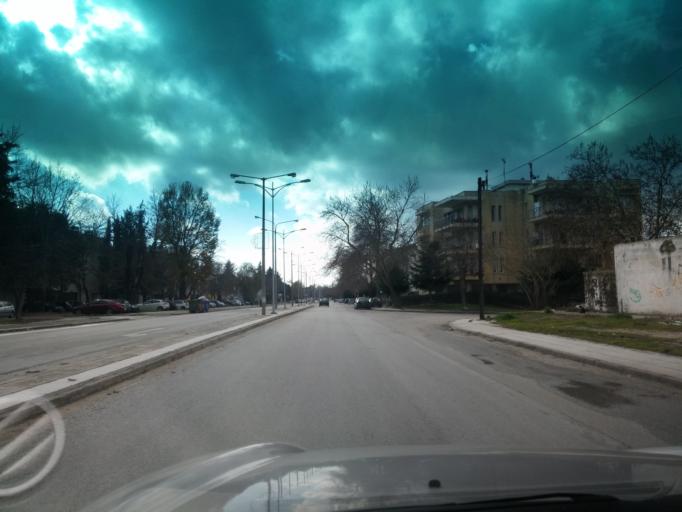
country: GR
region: East Macedonia and Thrace
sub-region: Nomos Rodopis
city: Komotini
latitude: 41.1251
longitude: 25.3924
